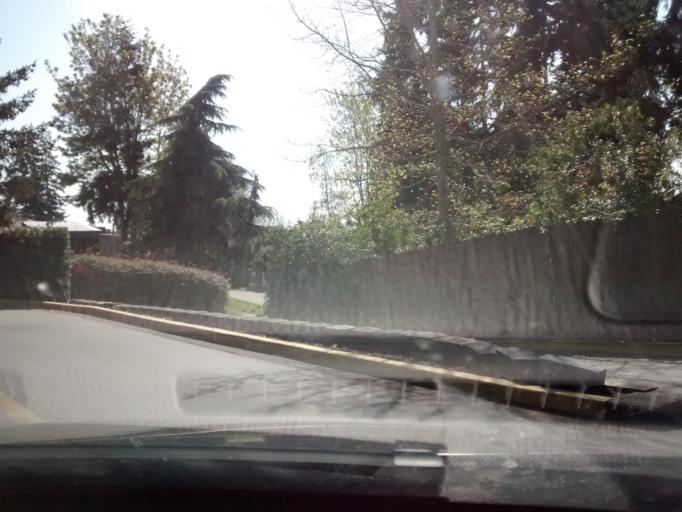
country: US
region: Washington
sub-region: Kitsap County
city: Kingston
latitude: 47.8010
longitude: -122.5011
